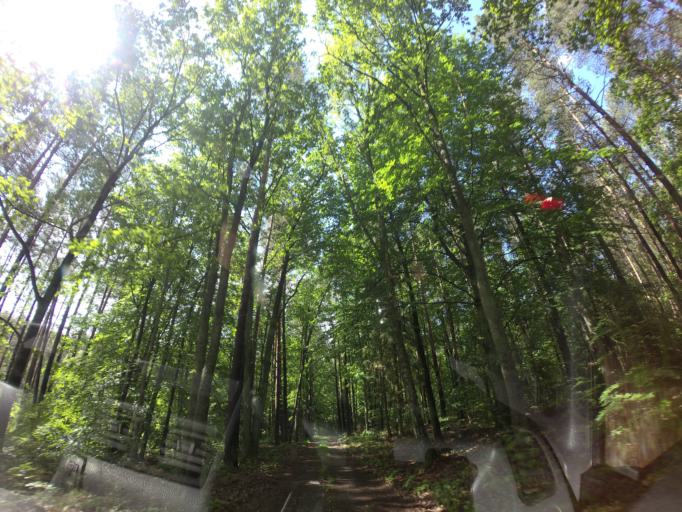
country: PL
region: West Pomeranian Voivodeship
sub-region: Powiat choszczenski
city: Drawno
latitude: 53.1824
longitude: 15.6724
